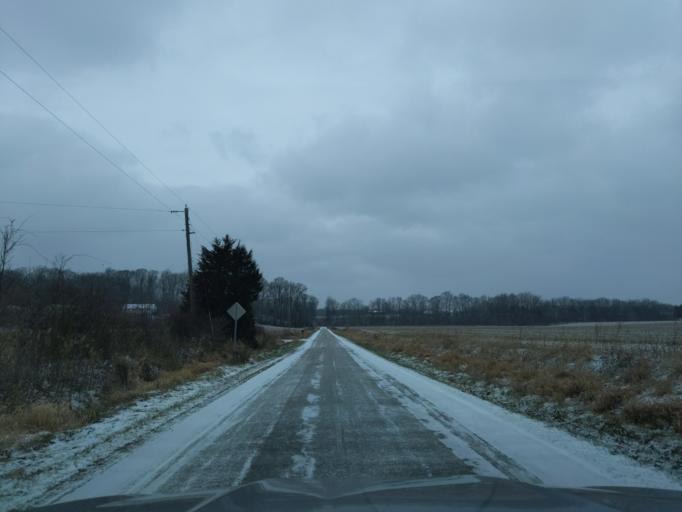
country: US
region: Indiana
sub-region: Decatur County
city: Greensburg
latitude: 39.2487
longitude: -85.4619
